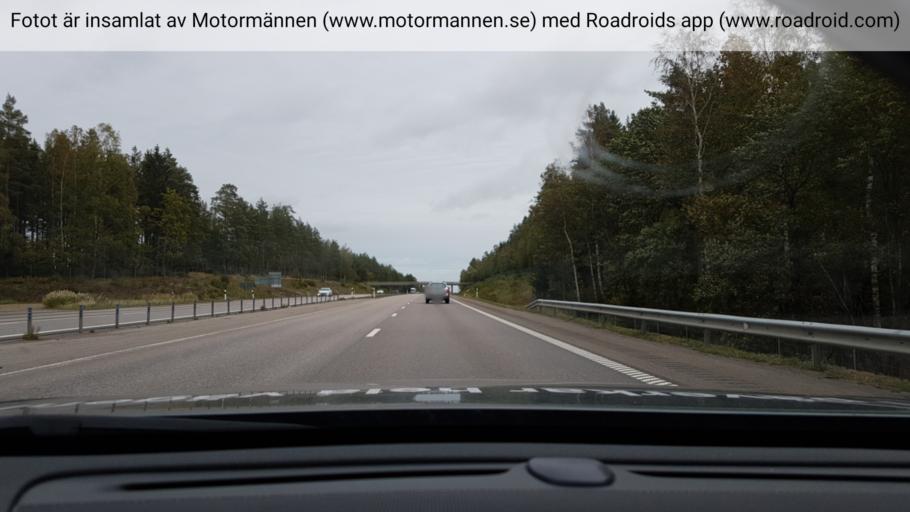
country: SE
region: OEstergoetland
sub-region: Mjolby Kommun
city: Mjolby
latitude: 58.3462
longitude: 15.1875
